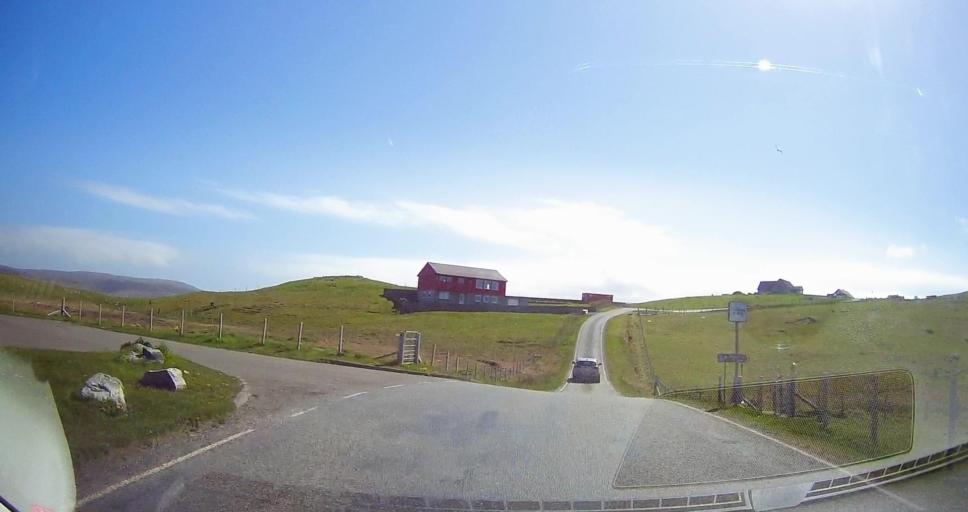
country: GB
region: Scotland
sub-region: Shetland Islands
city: Sandwick
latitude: 60.1023
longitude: -1.3240
